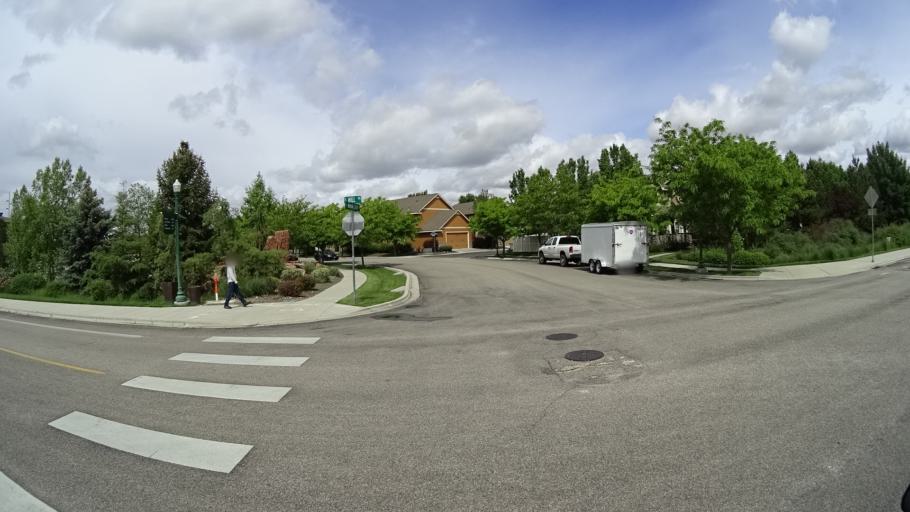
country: US
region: Idaho
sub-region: Ada County
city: Eagle
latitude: 43.6942
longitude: -116.3397
